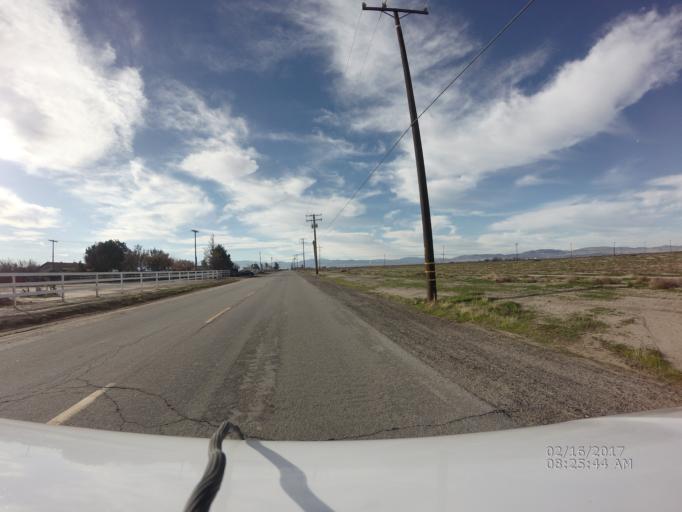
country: US
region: California
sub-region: Los Angeles County
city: Lancaster
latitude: 34.7059
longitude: -118.0055
